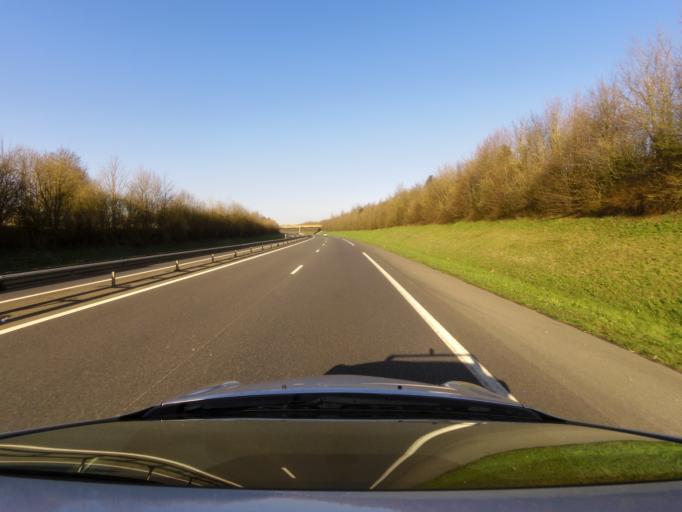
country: FR
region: Lower Normandy
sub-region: Departement du Calvados
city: Cahagnes
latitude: 49.0509
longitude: -0.7452
